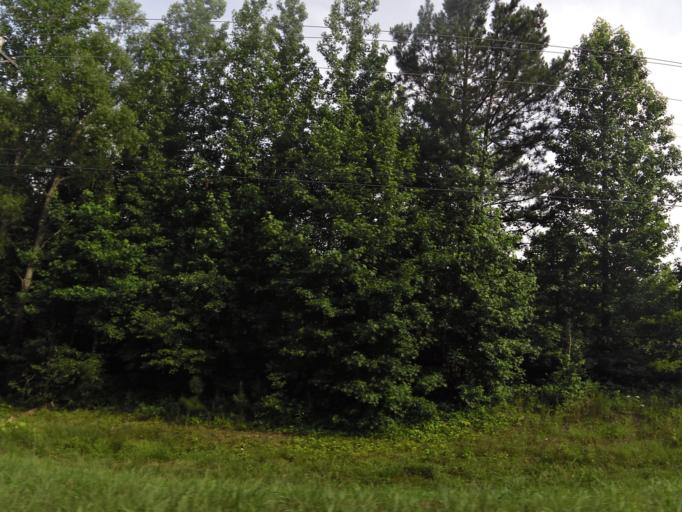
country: US
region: Tennessee
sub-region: Carroll County
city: Bruceton
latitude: 36.0446
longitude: -88.1753
